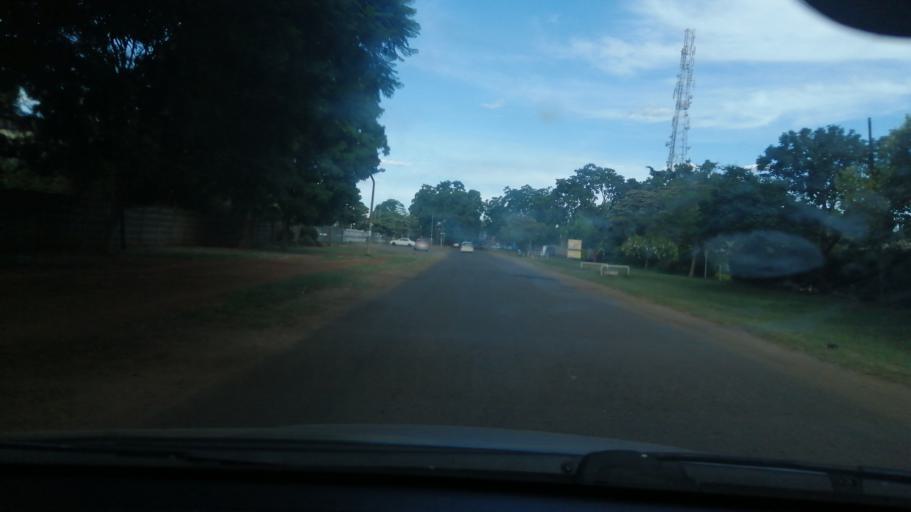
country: ZW
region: Harare
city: Harare
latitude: -17.7613
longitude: 31.0841
